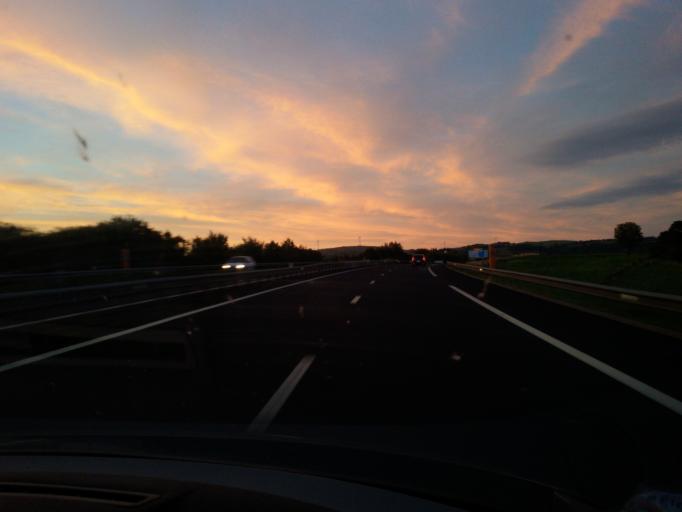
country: FR
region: Auvergne
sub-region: Departement du Cantal
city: Saint-Flour
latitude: 45.0618
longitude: 3.1106
